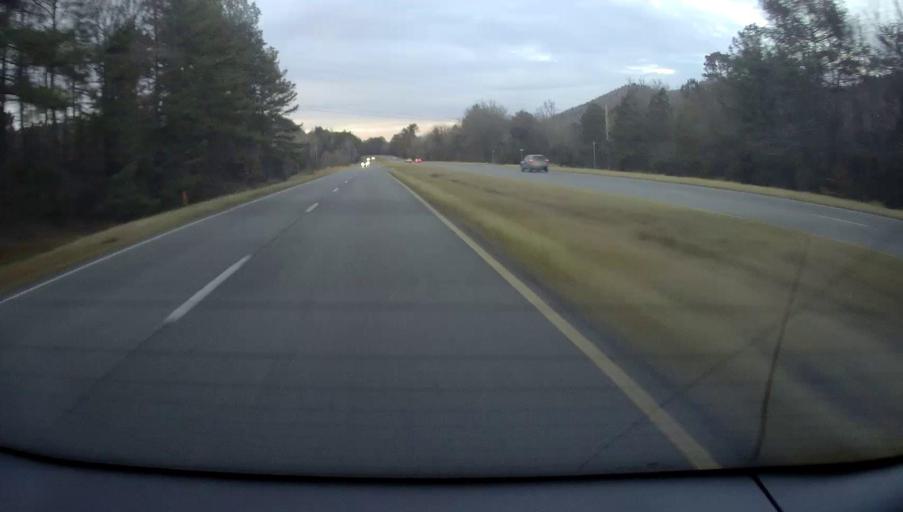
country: US
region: Alabama
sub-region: Etowah County
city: Glencoe
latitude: 33.9286
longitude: -85.9133
